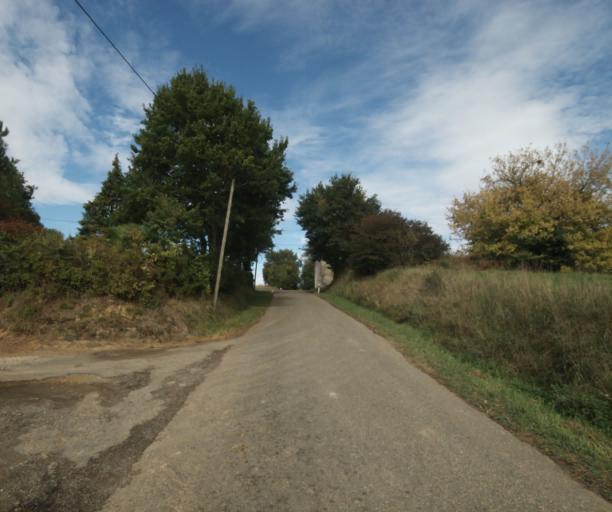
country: FR
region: Aquitaine
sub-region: Departement des Landes
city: Villeneuve-de-Marsan
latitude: 43.8938
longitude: -0.1974
